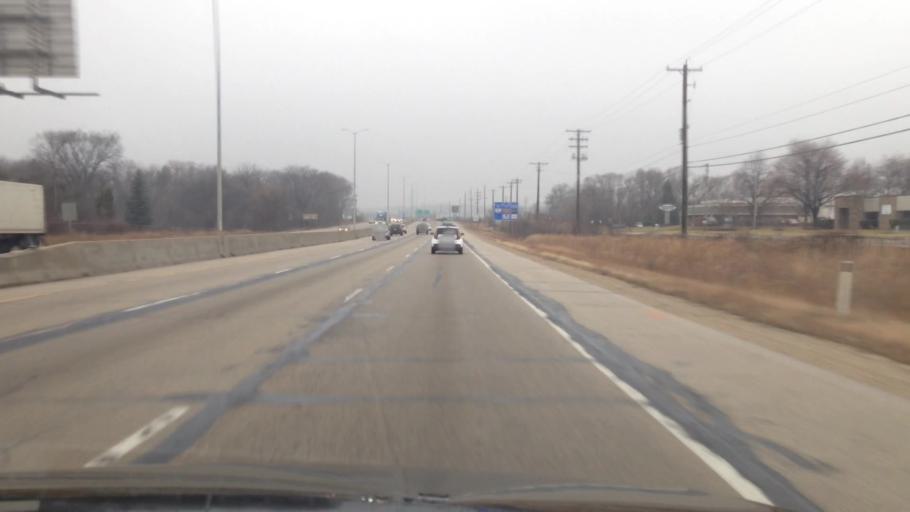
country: US
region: Wisconsin
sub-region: Waukesha County
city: Menomonee Falls
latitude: 43.1714
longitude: -88.0797
